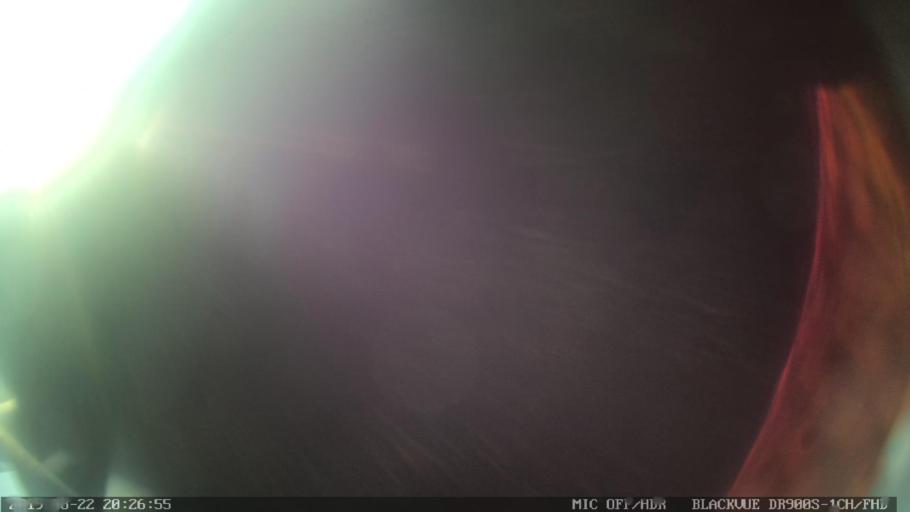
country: PT
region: Castelo Branco
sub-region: Castelo Branco
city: Castelo Branco
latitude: 39.7980
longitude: -7.5607
